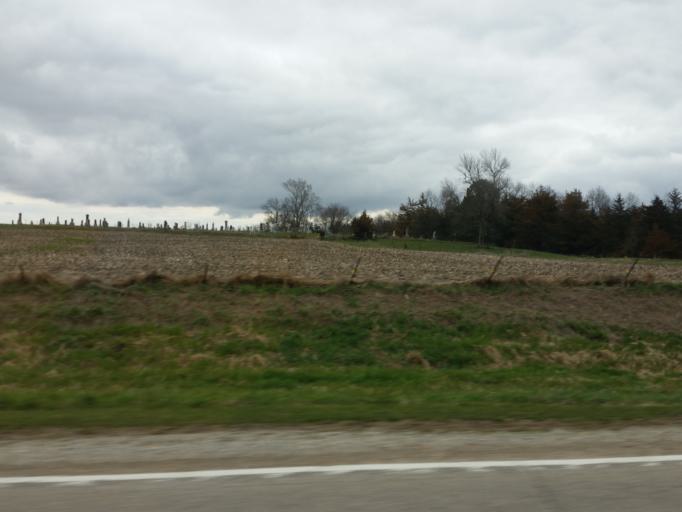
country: US
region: Iowa
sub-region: Benton County
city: Vinton
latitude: 42.3141
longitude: -91.9932
